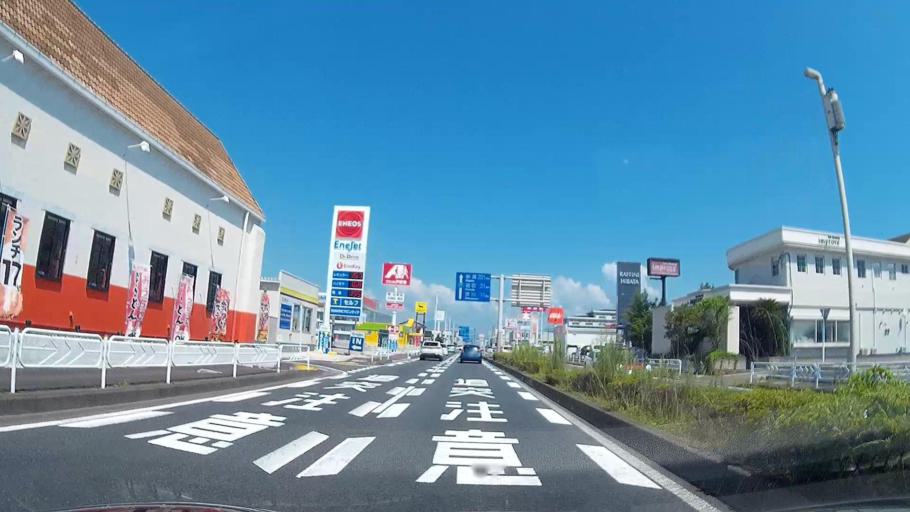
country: JP
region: Gunma
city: Maebashi-shi
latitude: 36.4254
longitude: 139.0570
